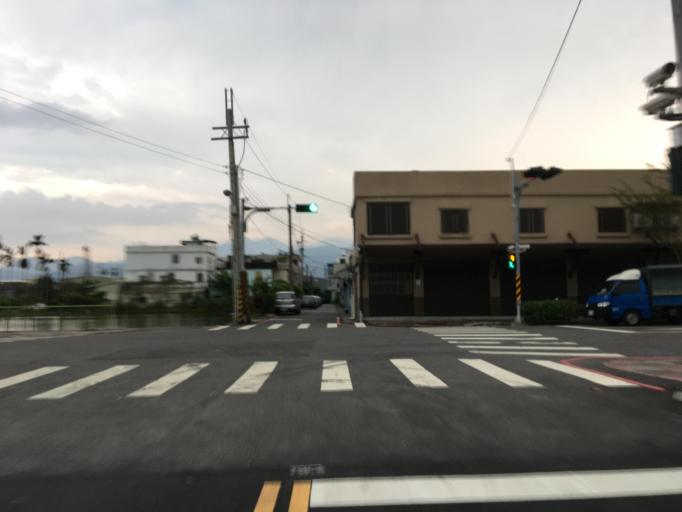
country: TW
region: Taiwan
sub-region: Yilan
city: Yilan
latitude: 24.6629
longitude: 121.7631
